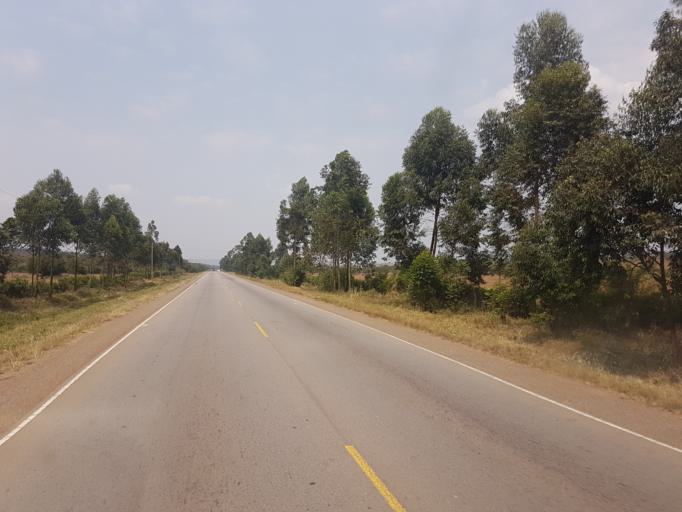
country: UG
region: Western Region
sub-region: Mbarara District
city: Mbarara
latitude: -0.5106
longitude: 30.7810
